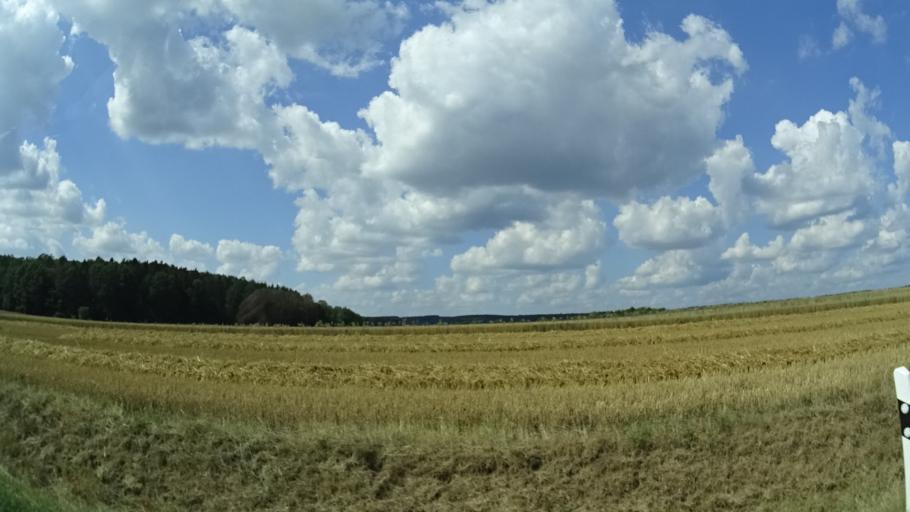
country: DE
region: Thuringia
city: Westhausen
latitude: 50.3688
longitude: 10.7009
